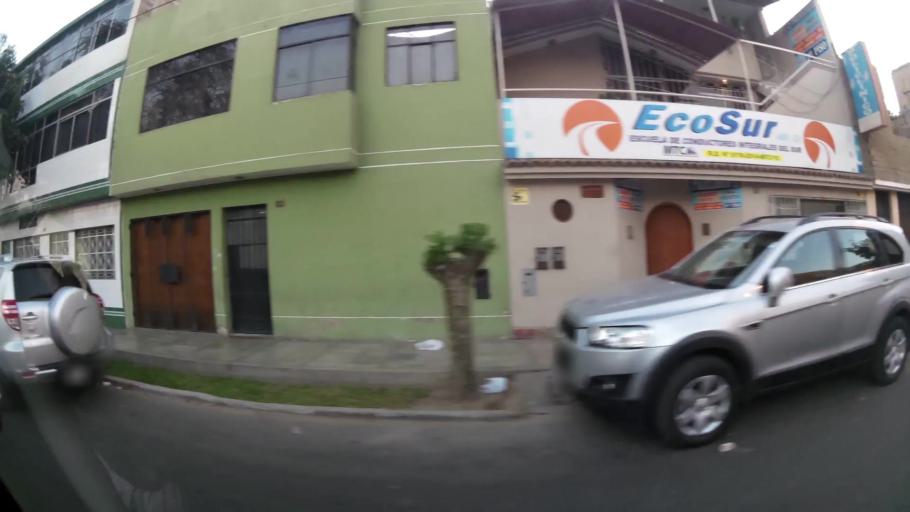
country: PE
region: Ica
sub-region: Provincia de Ica
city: Ica
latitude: -14.0680
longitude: -75.7327
